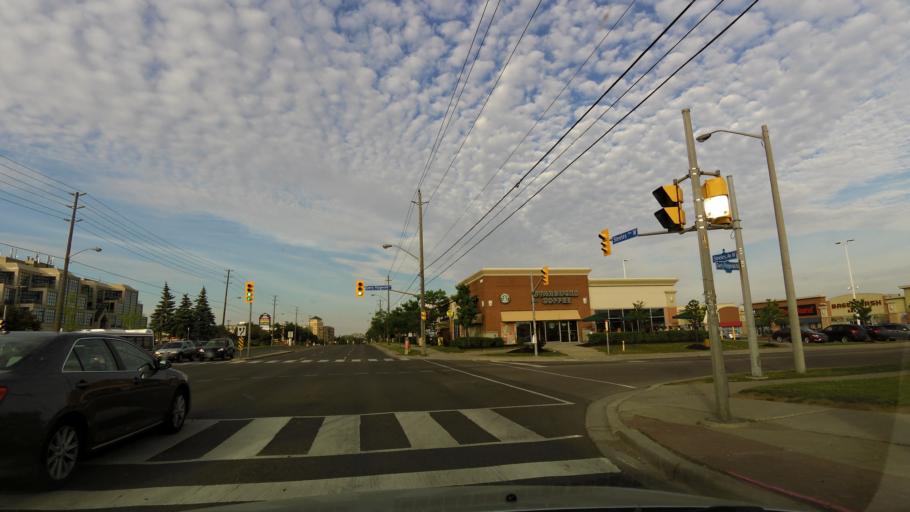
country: CA
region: Ontario
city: Concord
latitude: 43.7860
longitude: -79.4750
